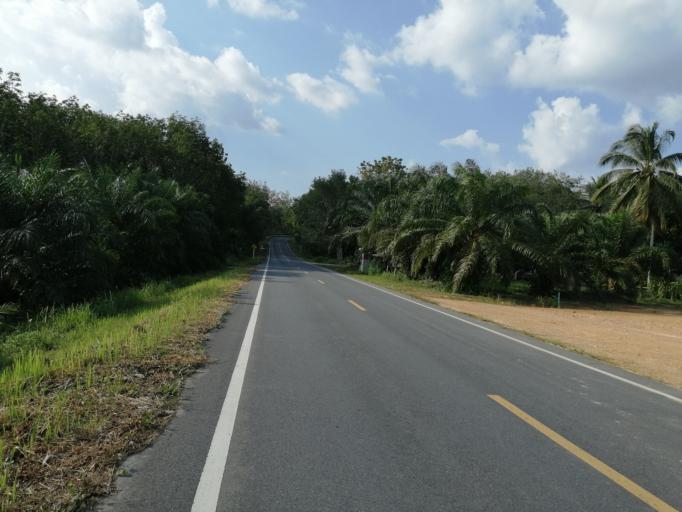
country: TH
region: Nakhon Si Thammarat
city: Na Bon
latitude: 8.2435
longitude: 99.6550
